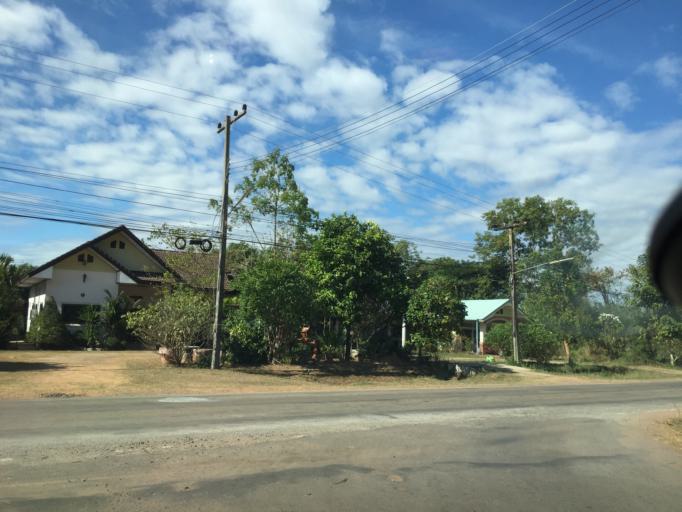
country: TH
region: Kalasin
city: Tha Khantho
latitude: 16.9714
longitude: 103.2658
